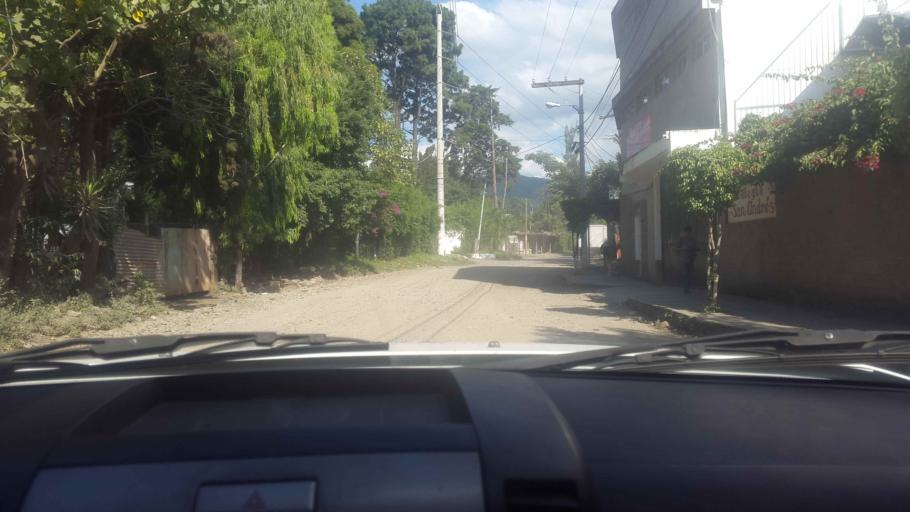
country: GT
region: Guatemala
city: Petapa
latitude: 14.5157
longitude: -90.5422
